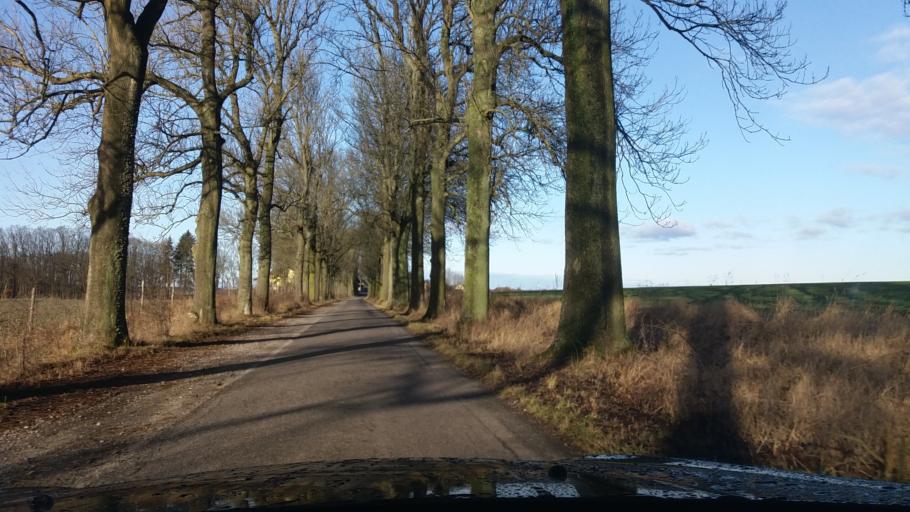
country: PL
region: West Pomeranian Voivodeship
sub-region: Powiat choszczenski
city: Drawno
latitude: 53.1900
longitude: 15.7921
